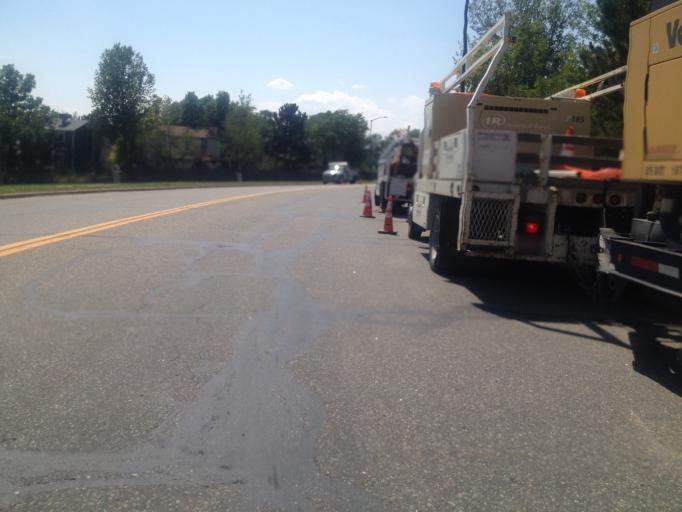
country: US
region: Colorado
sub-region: Boulder County
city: Louisville
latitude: 39.9747
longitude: -105.1465
